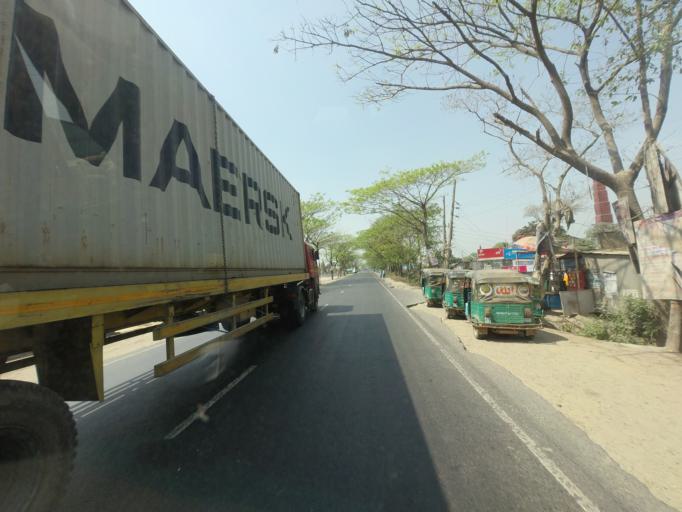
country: BD
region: Dhaka
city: Bhairab Bazar
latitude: 24.0447
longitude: 91.0671
